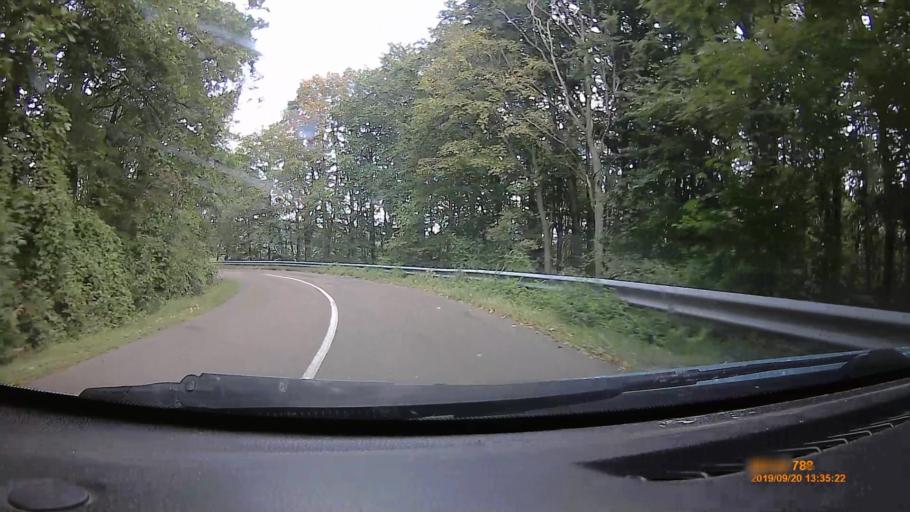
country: HU
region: Heves
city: Szilvasvarad
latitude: 48.0512
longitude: 20.5131
